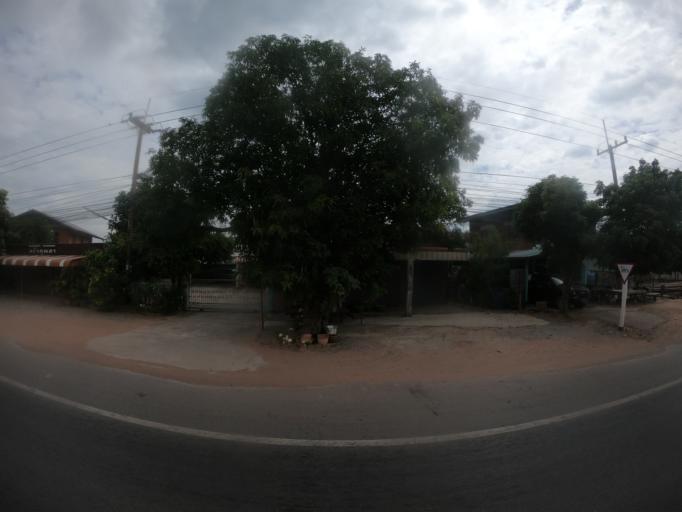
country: TH
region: Maha Sarakham
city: Kantharawichai
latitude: 16.2647
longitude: 103.2832
